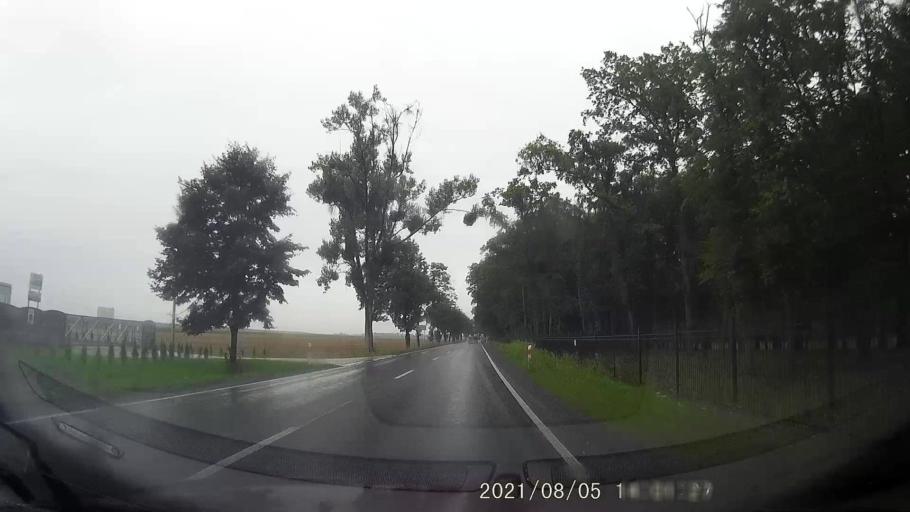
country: PL
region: Opole Voivodeship
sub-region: Powiat krapkowicki
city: Strzeleczki
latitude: 50.4480
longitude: 17.8929
